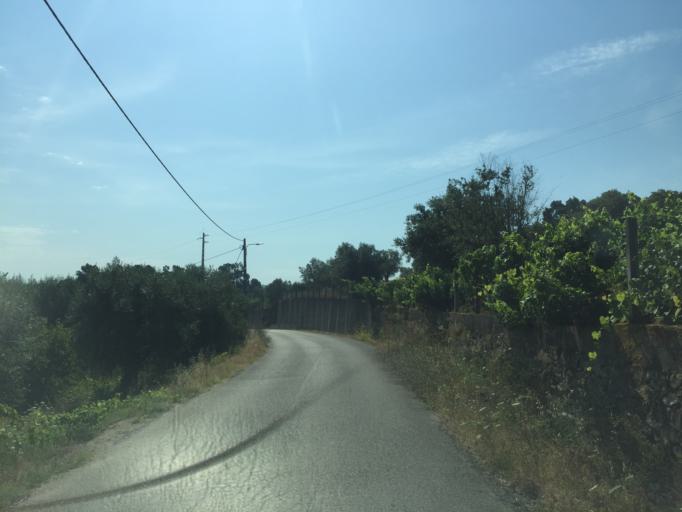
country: PT
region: Santarem
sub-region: Ferreira do Zezere
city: Ferreira do Zezere
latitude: 39.6068
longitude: -8.2851
